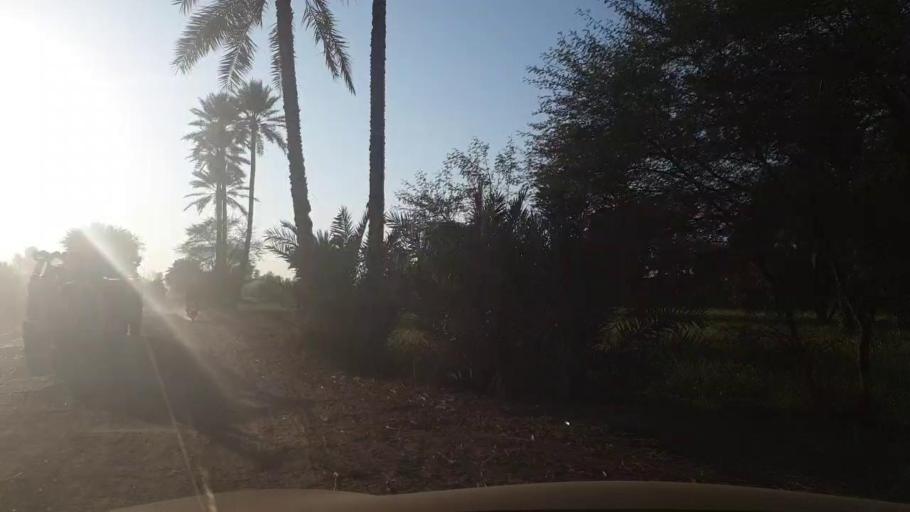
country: PK
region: Sindh
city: Ghotki
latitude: 28.0684
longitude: 69.3555
